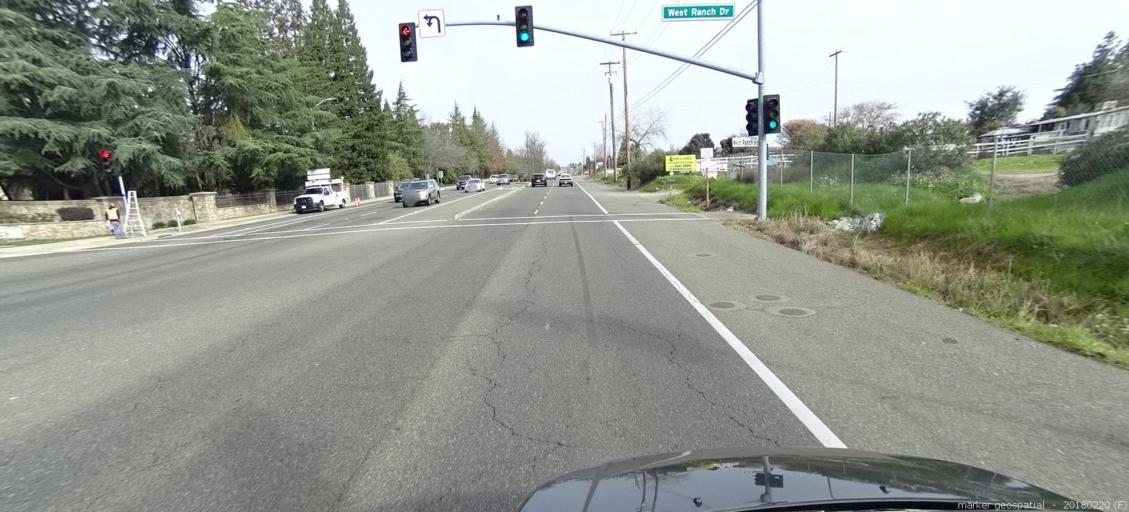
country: US
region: California
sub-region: Sacramento County
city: Orangevale
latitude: 38.7161
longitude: -121.2258
